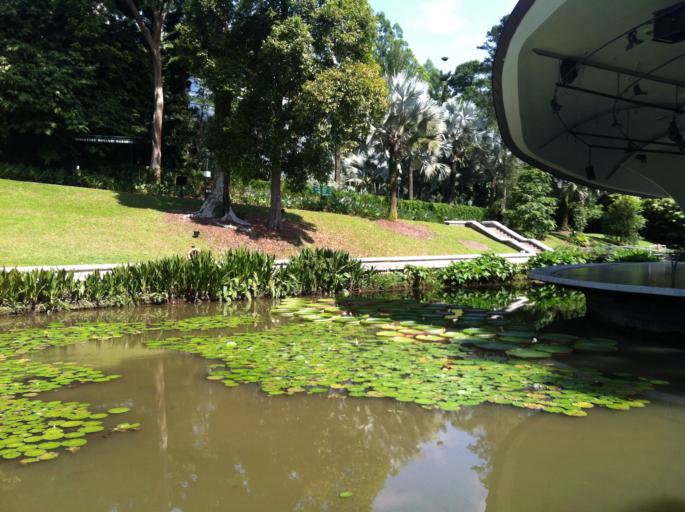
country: SG
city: Singapore
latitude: 1.3137
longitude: 103.8152
